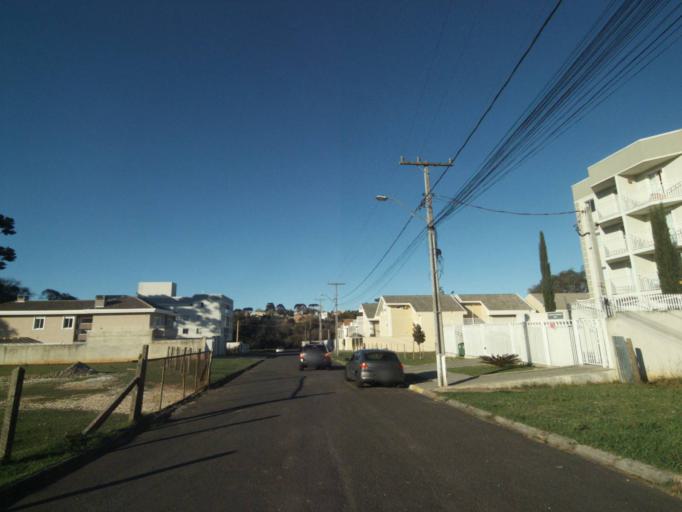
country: BR
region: Parana
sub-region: Curitiba
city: Curitiba
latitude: -25.3857
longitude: -49.2455
